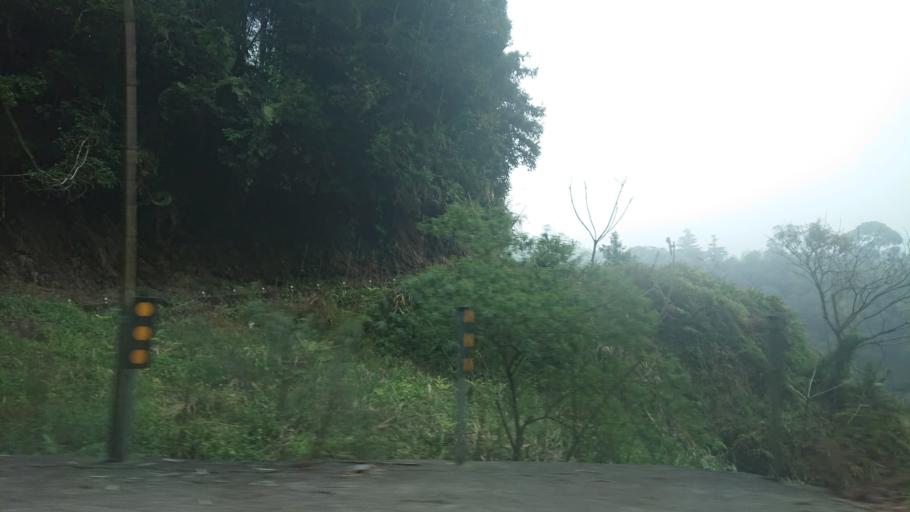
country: TW
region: Taiwan
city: Lugu
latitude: 23.6188
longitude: 120.7200
